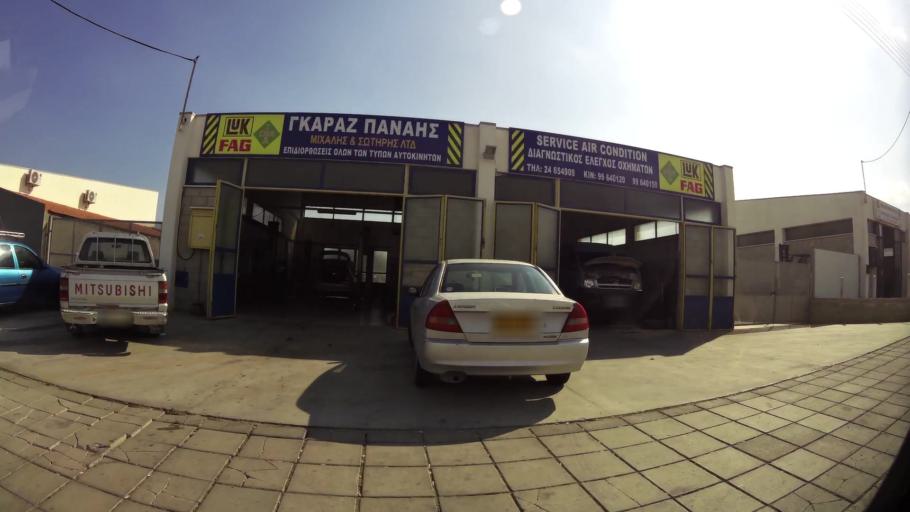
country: CY
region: Larnaka
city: Dhromolaxia
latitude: 34.9013
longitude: 33.5778
